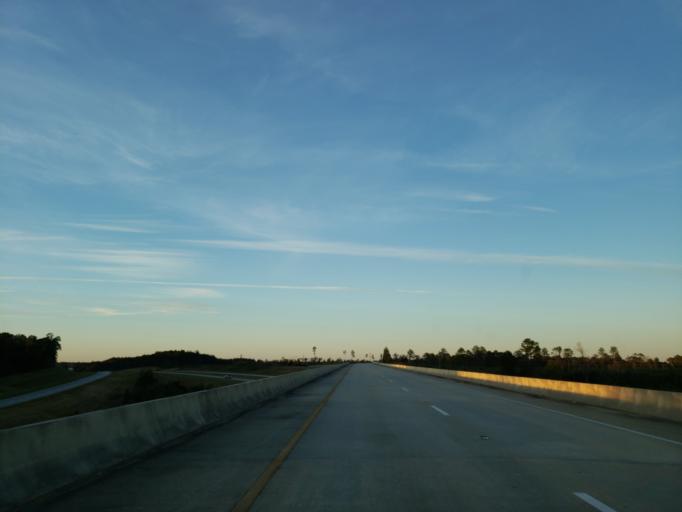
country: US
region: Mississippi
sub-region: Wayne County
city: Belmont
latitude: 31.4522
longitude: -88.4646
